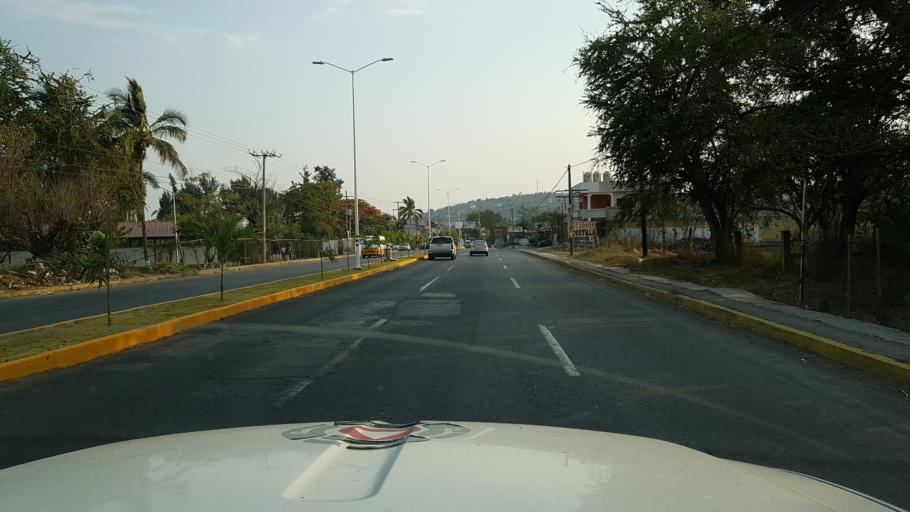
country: MX
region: Morelos
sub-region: Ayala
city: San Pedro Apatlaco
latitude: 18.7868
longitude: -98.9787
